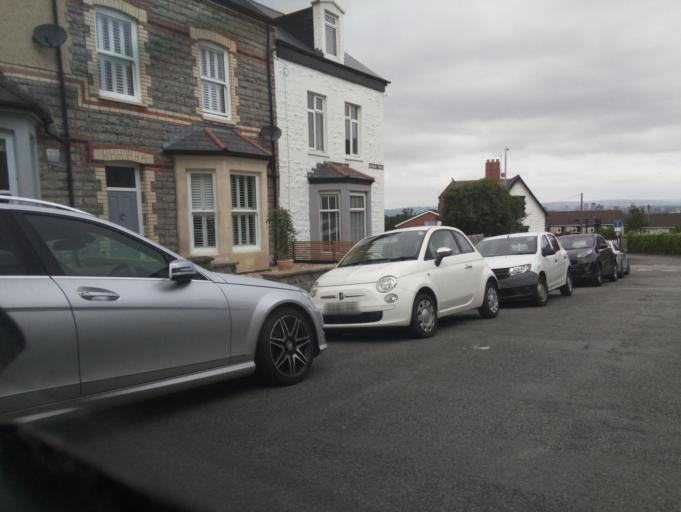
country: GB
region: Wales
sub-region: Vale of Glamorgan
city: Penarth
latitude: 51.4435
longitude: -3.1700
